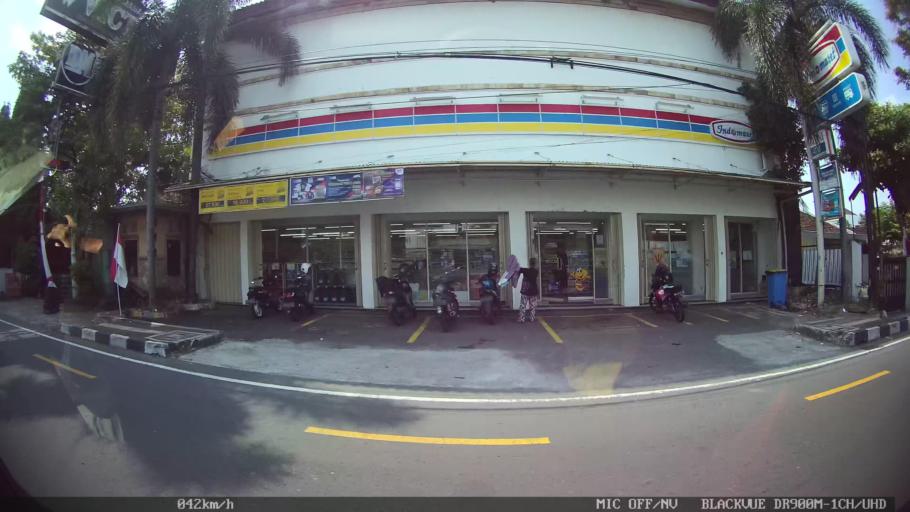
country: ID
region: Daerah Istimewa Yogyakarta
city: Yogyakarta
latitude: -7.8041
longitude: 110.3949
